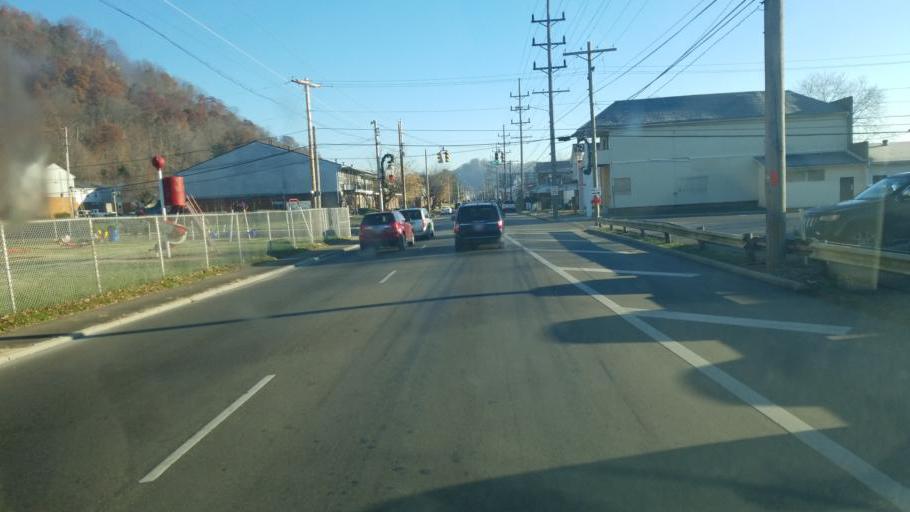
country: US
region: Ohio
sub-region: Scioto County
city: New Boston
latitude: 38.7481
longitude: -82.9429
